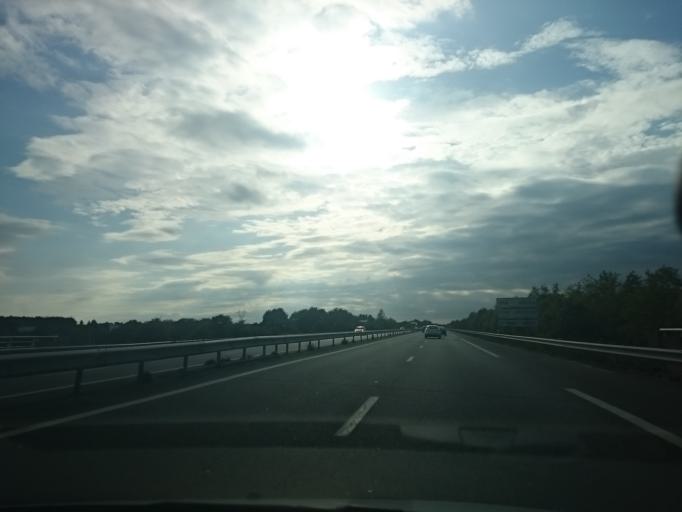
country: FR
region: Pays de la Loire
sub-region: Departement de la Loire-Atlantique
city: Besne
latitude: 47.4177
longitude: -2.0383
